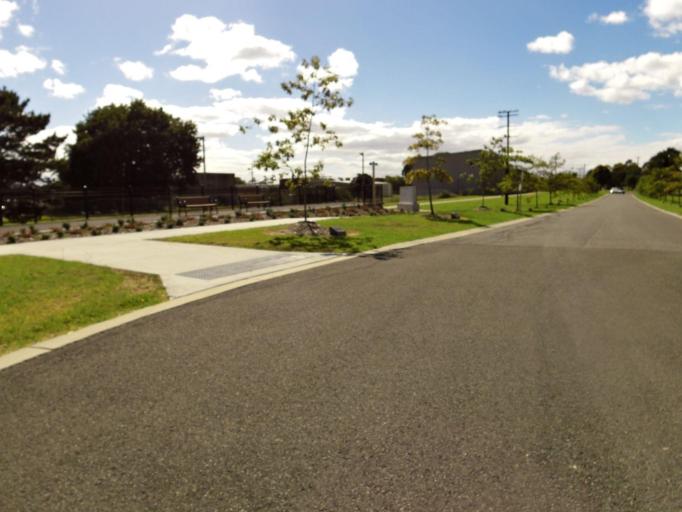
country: AU
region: Victoria
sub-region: Cardinia
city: Koo-Wee-Rup
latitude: -38.1994
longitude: 145.4875
